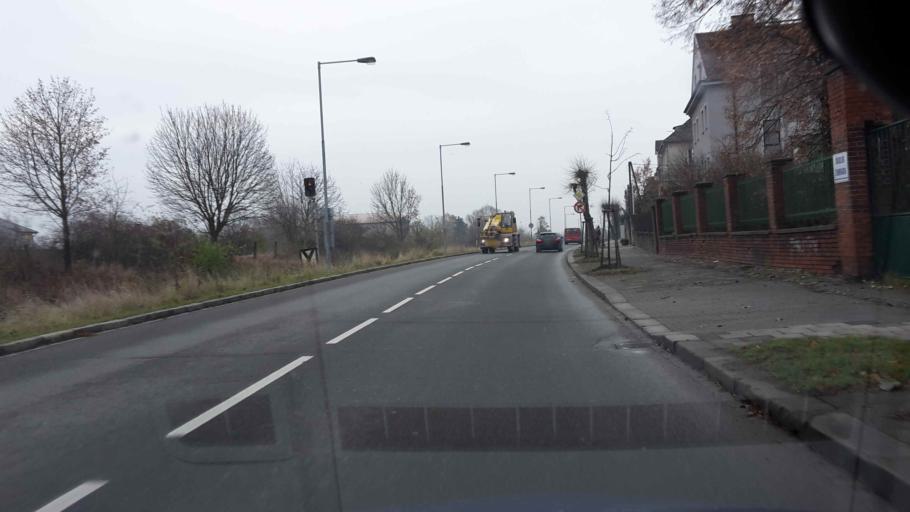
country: CZ
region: Olomoucky
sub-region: Okres Olomouc
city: Olomouc
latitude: 49.6040
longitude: 17.2340
